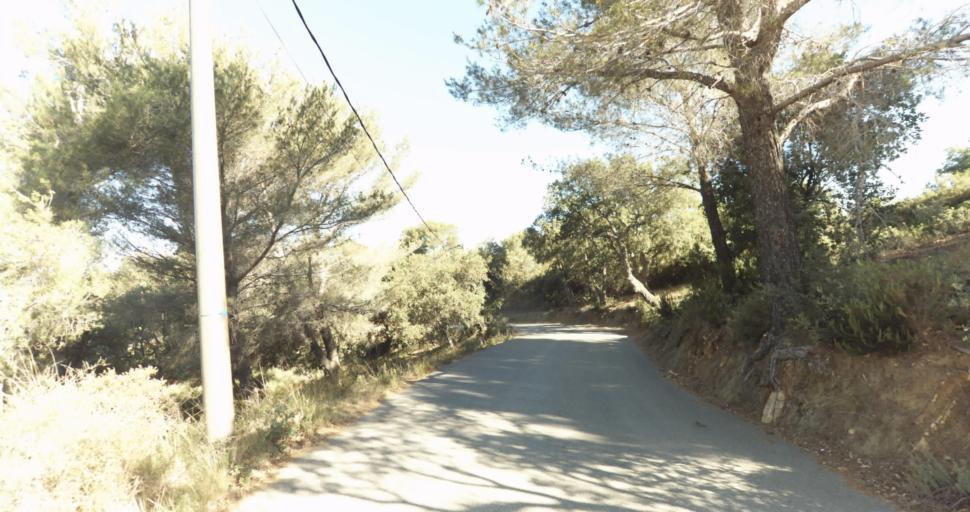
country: FR
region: Provence-Alpes-Cote d'Azur
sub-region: Departement du Var
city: Gassin
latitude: 43.2156
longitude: 6.5867
